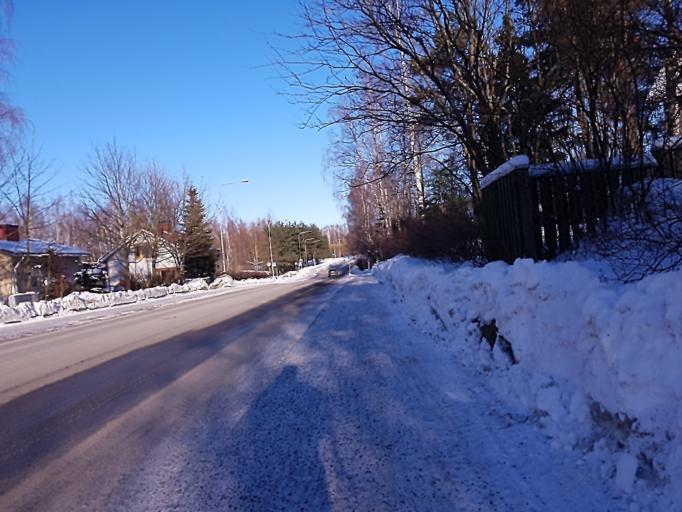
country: FI
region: Uusimaa
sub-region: Helsinki
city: Teekkarikylae
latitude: 60.2456
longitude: 24.8819
